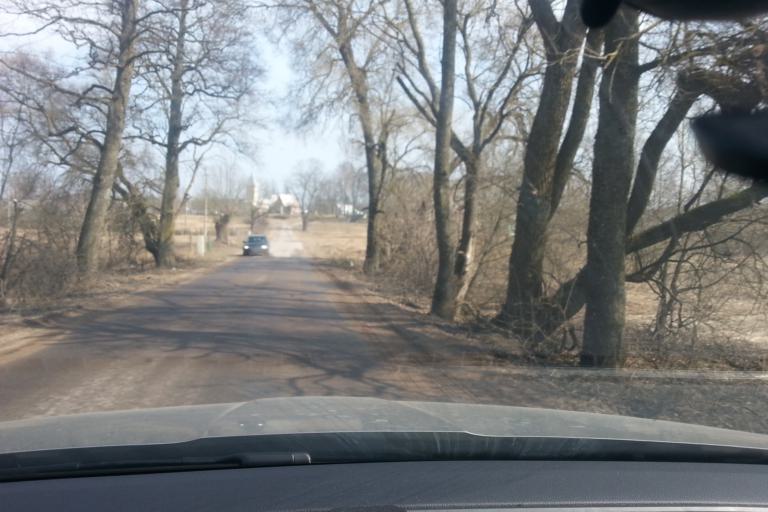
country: LT
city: Trakai
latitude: 54.5001
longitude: 24.9820
